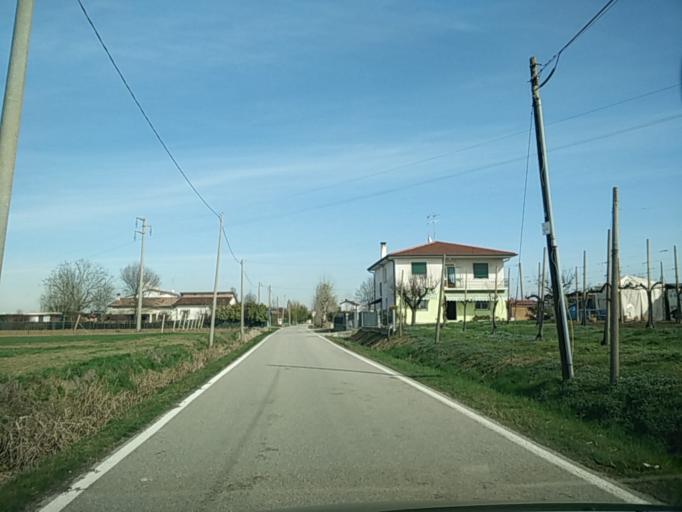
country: IT
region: Veneto
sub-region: Provincia di Treviso
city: Biancade
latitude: 45.6593
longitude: 12.3425
